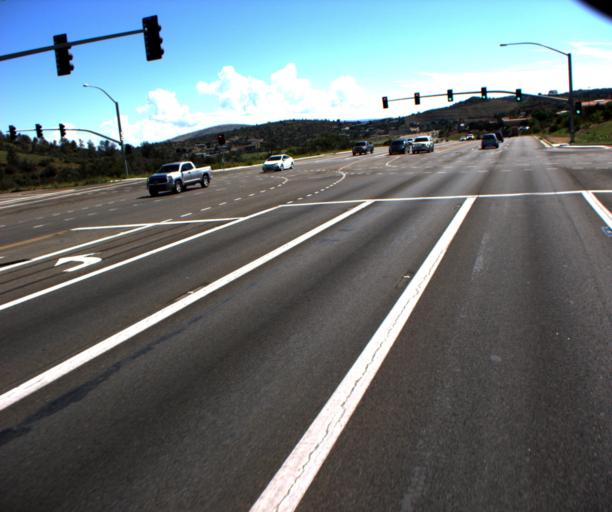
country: US
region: Arizona
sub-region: Yavapai County
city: Prescott
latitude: 34.5495
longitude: -112.4386
